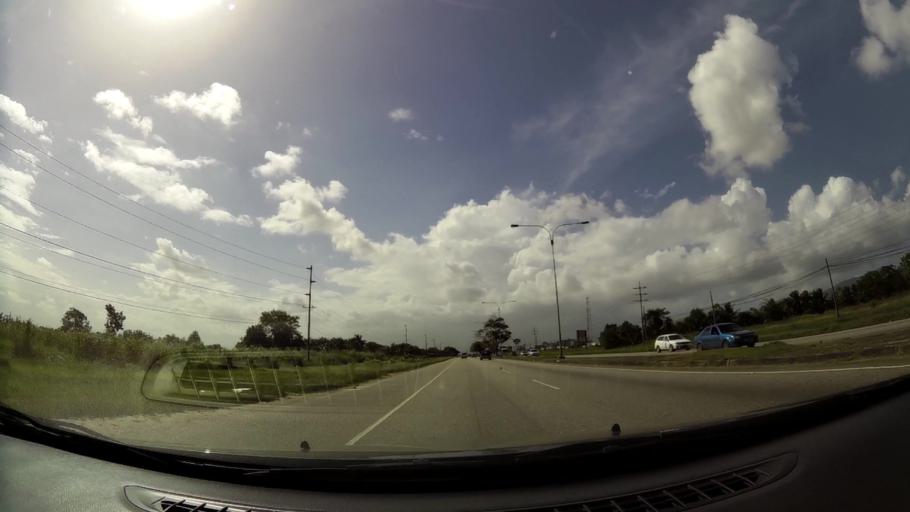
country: TT
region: Borough of Arima
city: Arima
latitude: 10.6136
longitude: -61.3042
